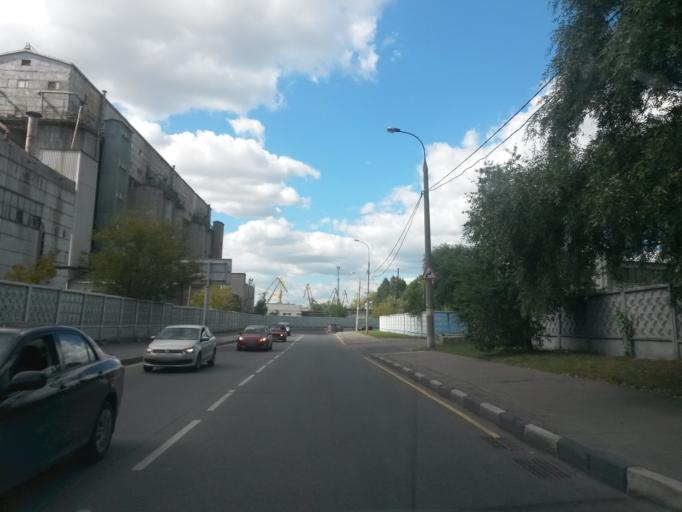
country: RU
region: Moscow
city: Tekstil'shchiki
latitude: 55.6917
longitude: 37.7167
